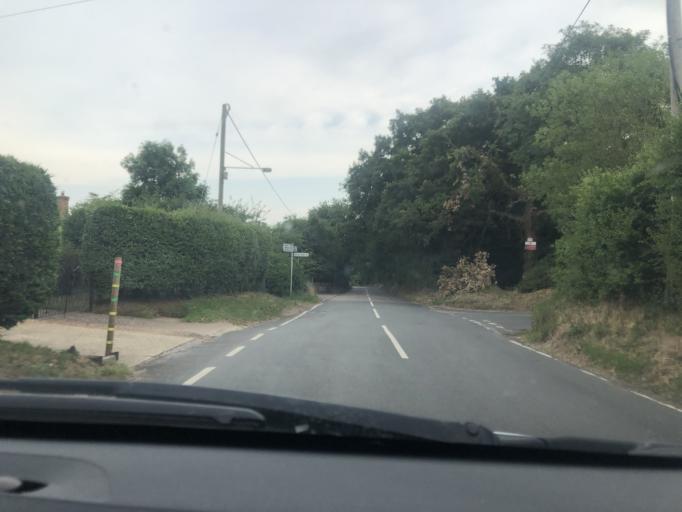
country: GB
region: England
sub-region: Kent
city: Sturry
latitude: 51.3101
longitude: 1.1362
